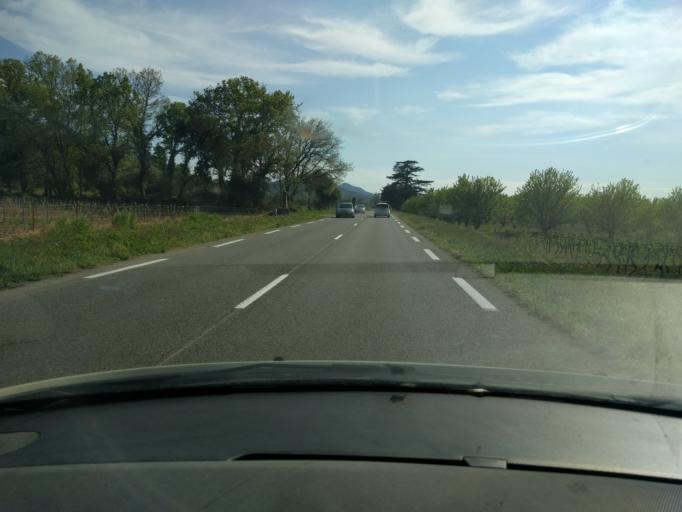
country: FR
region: Provence-Alpes-Cote d'Azur
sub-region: Departement du Var
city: Pierrefeu-du-Var
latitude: 43.1866
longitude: 6.1217
